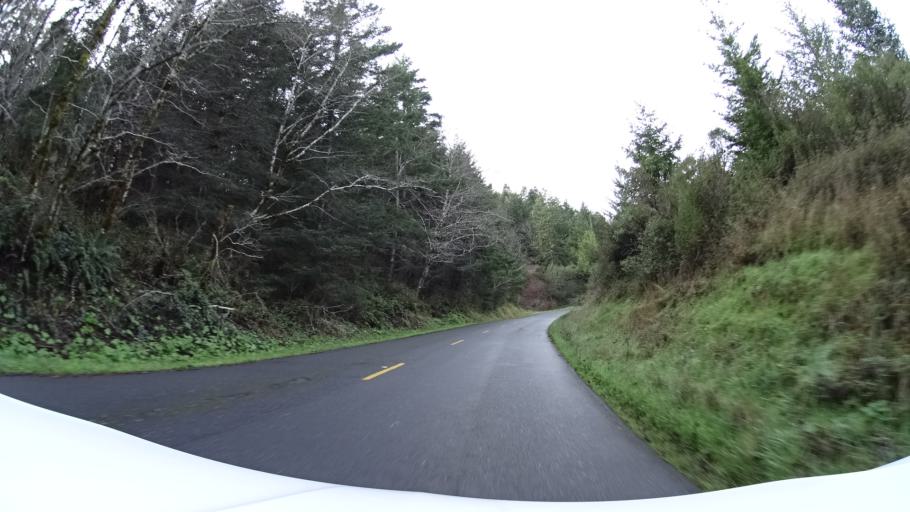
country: US
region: California
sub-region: Humboldt County
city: Ferndale
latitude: 40.3452
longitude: -124.3416
